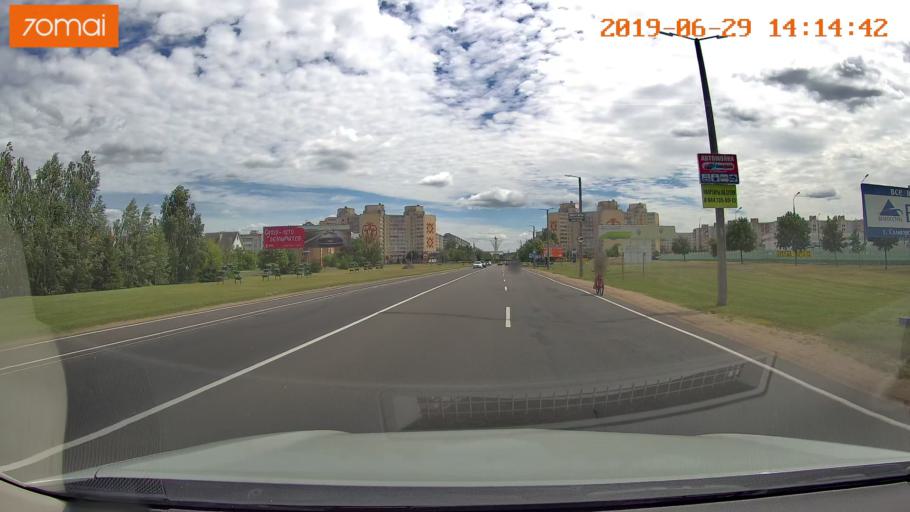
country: BY
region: Minsk
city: Salihorsk
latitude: 52.7939
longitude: 27.5176
